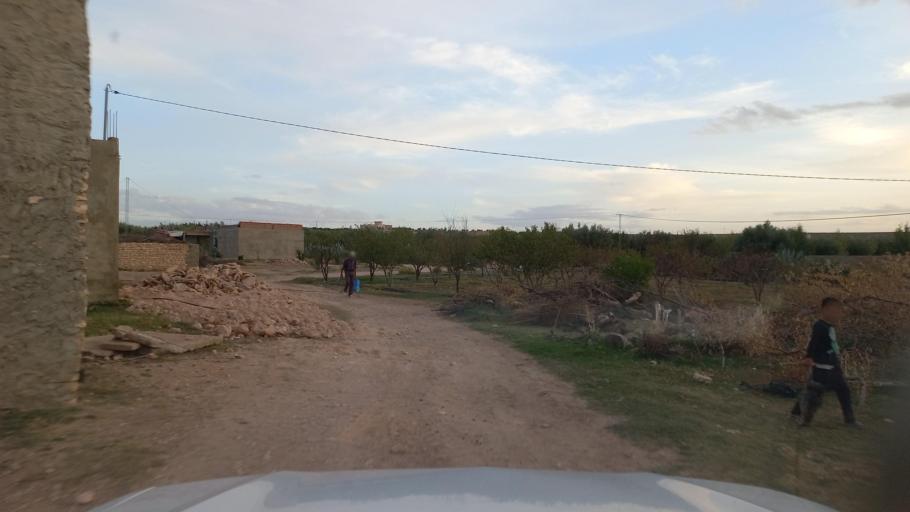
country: TN
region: Al Qasrayn
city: Sbiba
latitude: 35.4123
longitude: 9.1028
